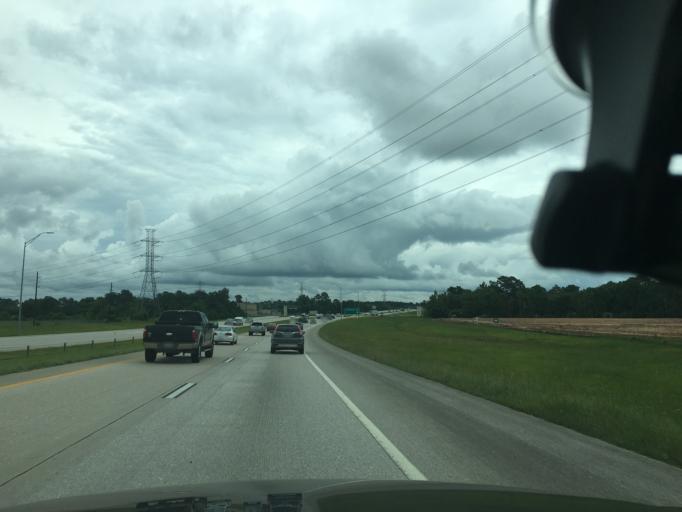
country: US
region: Texas
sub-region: Montgomery County
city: The Woodlands
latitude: 30.0927
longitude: -95.5150
